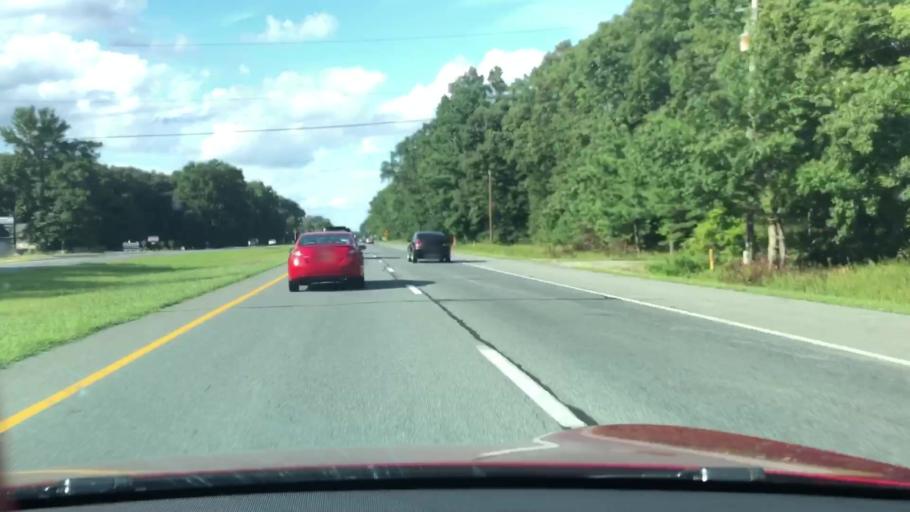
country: US
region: Delaware
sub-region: Kent County
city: Woodside East
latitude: 39.0645
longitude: -75.5542
